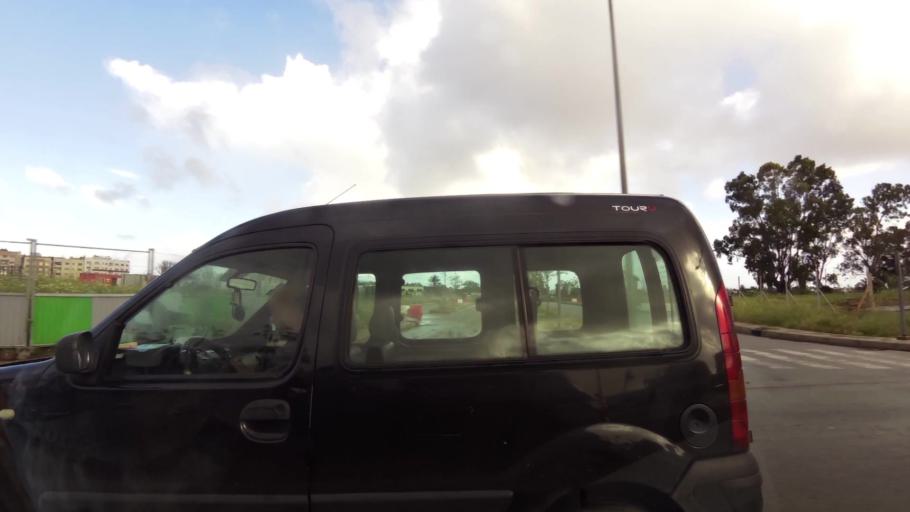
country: MA
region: Grand Casablanca
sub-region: Casablanca
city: Casablanca
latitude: 33.5636
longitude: -7.6646
